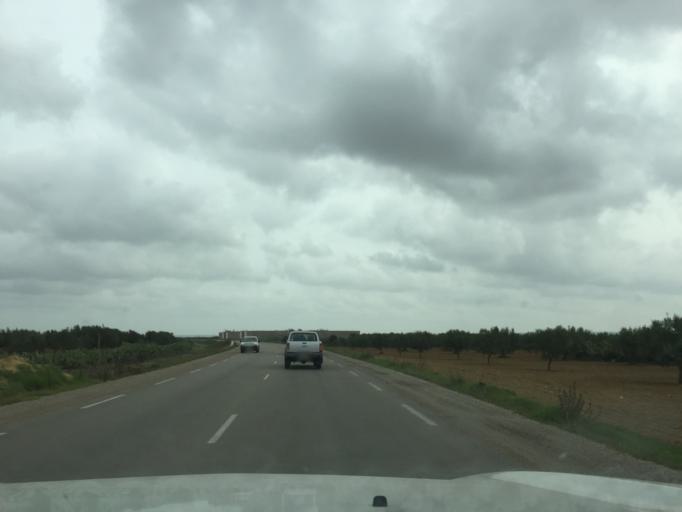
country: TN
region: Al Munastir
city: Manzil Kamil
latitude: 35.6147
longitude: 10.6702
